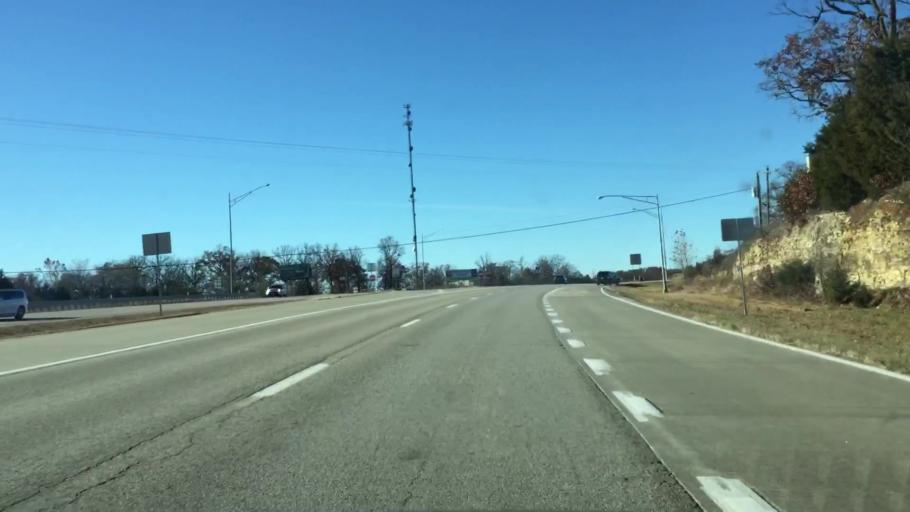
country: US
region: Missouri
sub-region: Cole County
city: Wardsville
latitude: 38.4742
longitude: -92.2776
